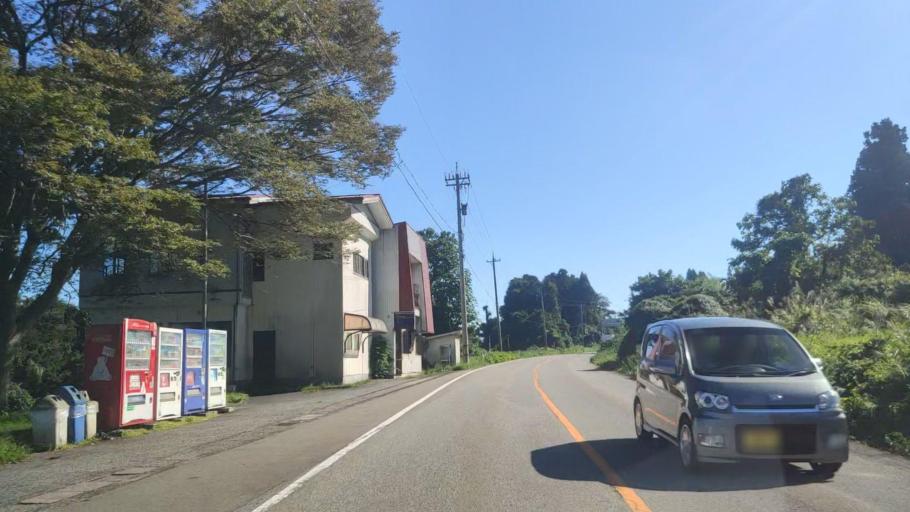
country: JP
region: Ishikawa
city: Nanao
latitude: 37.2700
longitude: 137.0949
